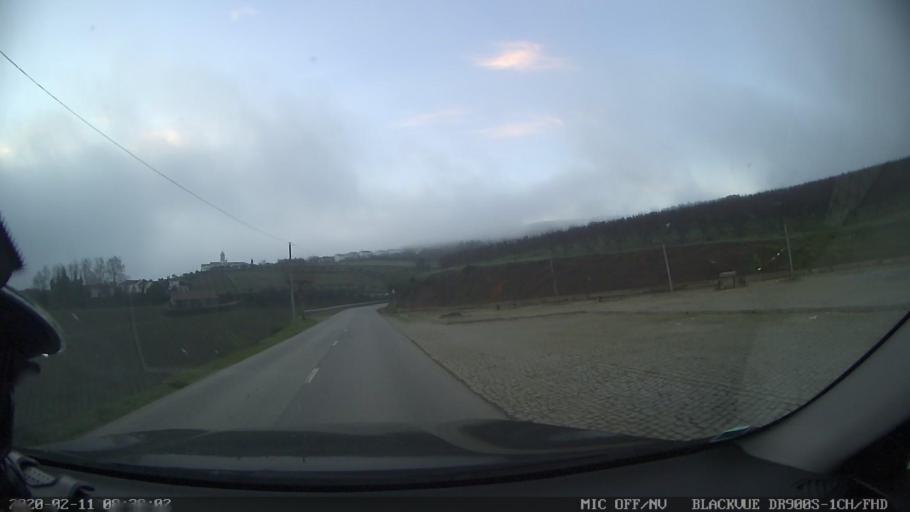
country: PT
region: Vila Real
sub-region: Sabrosa
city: Sabrosa
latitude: 41.2514
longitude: -7.5852
